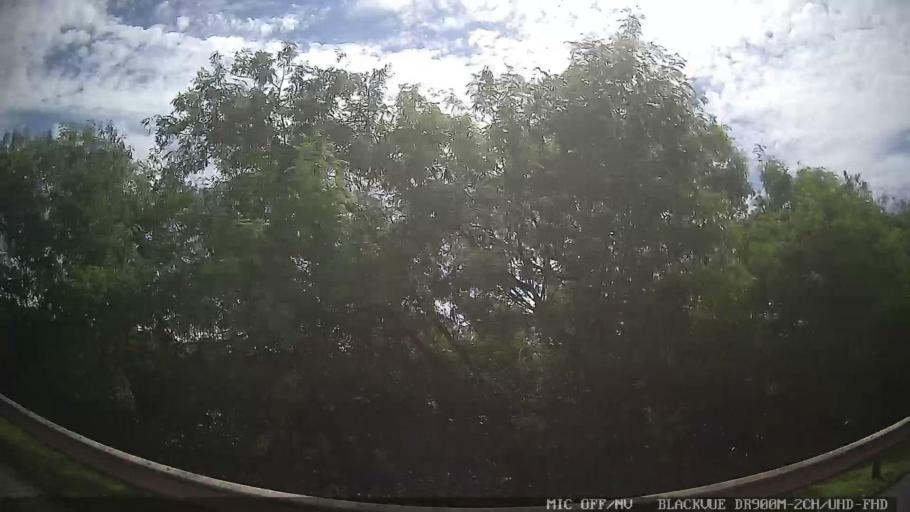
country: BR
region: Sao Paulo
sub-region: Laranjal Paulista
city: Laranjal Paulista
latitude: -23.0634
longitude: -47.8217
